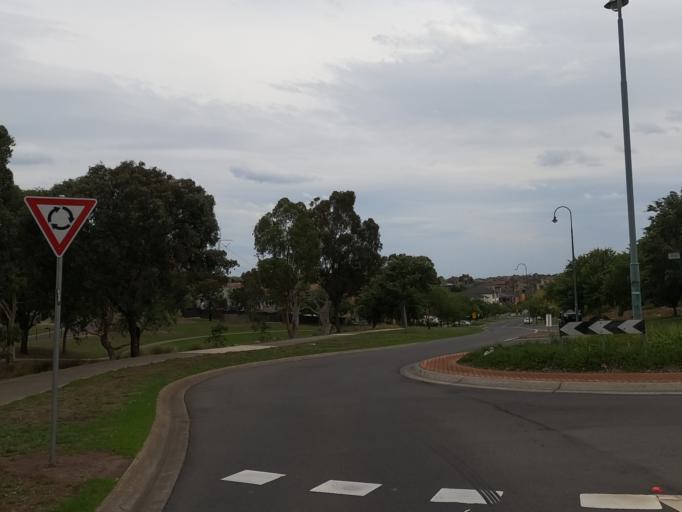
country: AU
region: Victoria
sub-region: Hume
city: Meadow Heights
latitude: -37.6404
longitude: 144.9087
